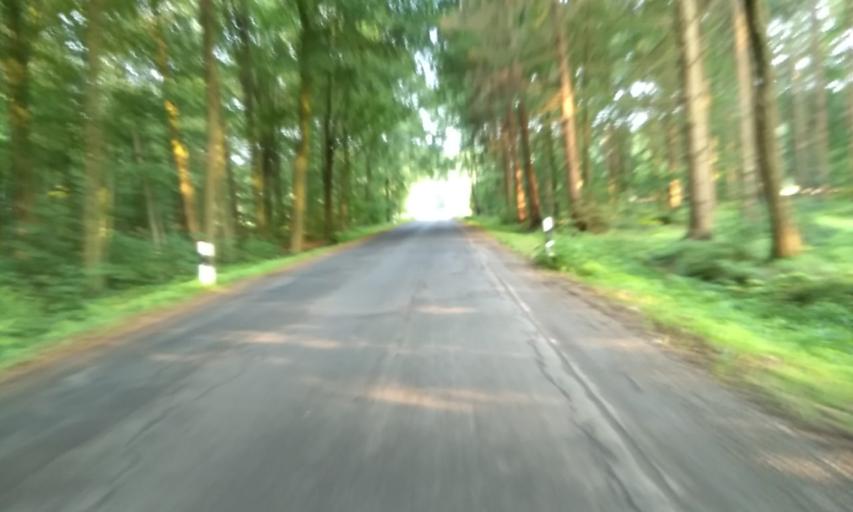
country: DE
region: Lower Saxony
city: Harsefeld
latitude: 53.4096
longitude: 9.5143
